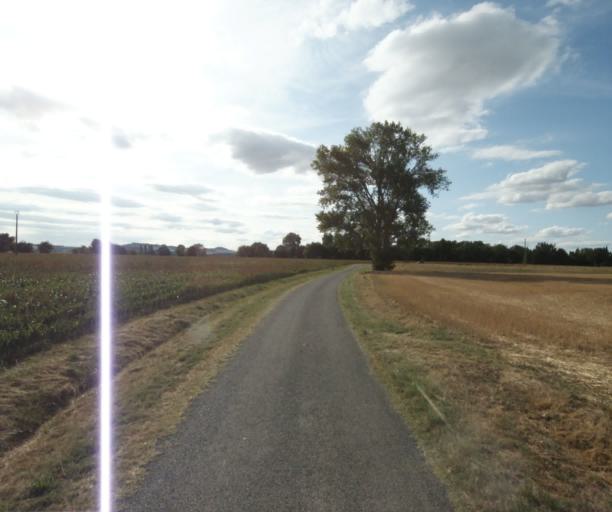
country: FR
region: Midi-Pyrenees
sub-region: Departement de la Haute-Garonne
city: Revel
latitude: 43.5142
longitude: 1.9924
